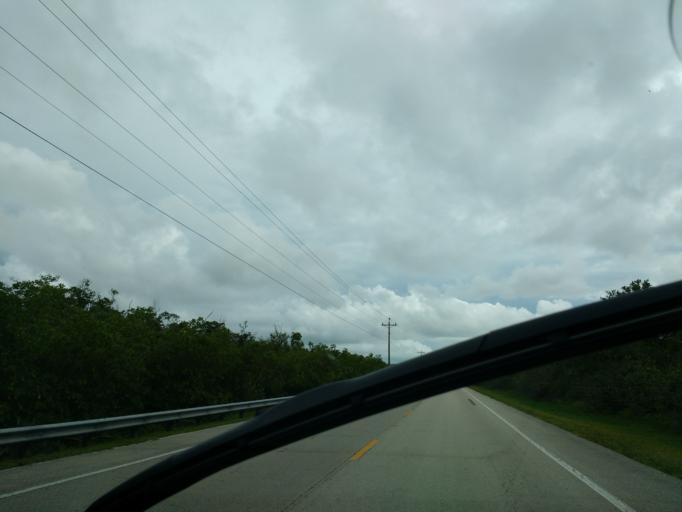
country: US
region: Florida
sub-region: Collier County
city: Marco
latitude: 25.8788
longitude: -81.3803
